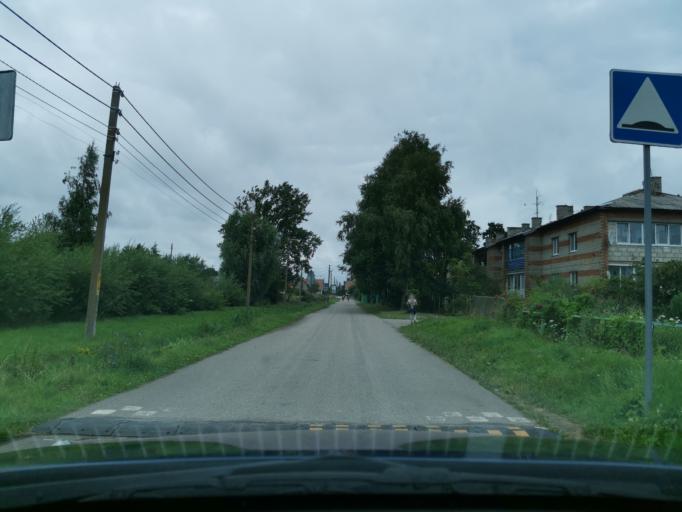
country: LT
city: Nida
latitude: 55.1524
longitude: 20.8519
